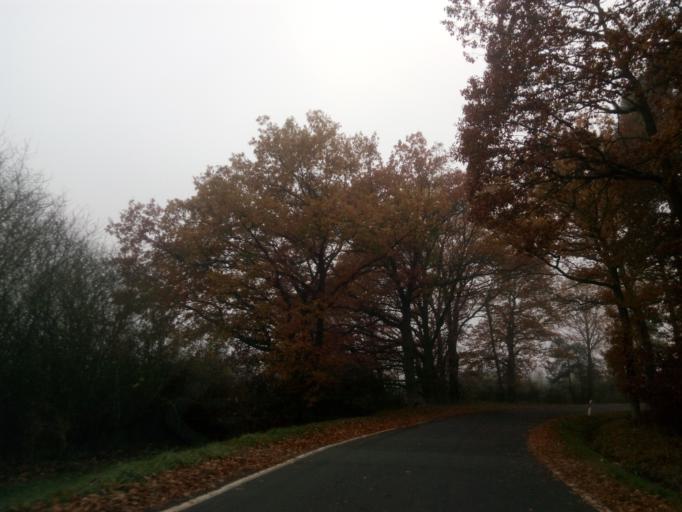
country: DE
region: Rheinland-Pfalz
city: Sienhachenbach
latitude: 49.7022
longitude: 7.4757
